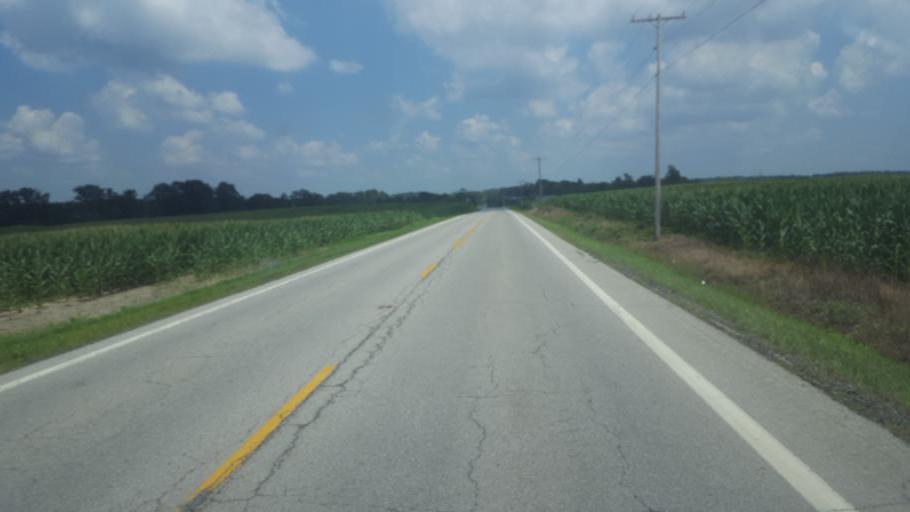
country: US
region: Ohio
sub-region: Crawford County
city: Crestline
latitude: 40.7522
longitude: -82.7182
